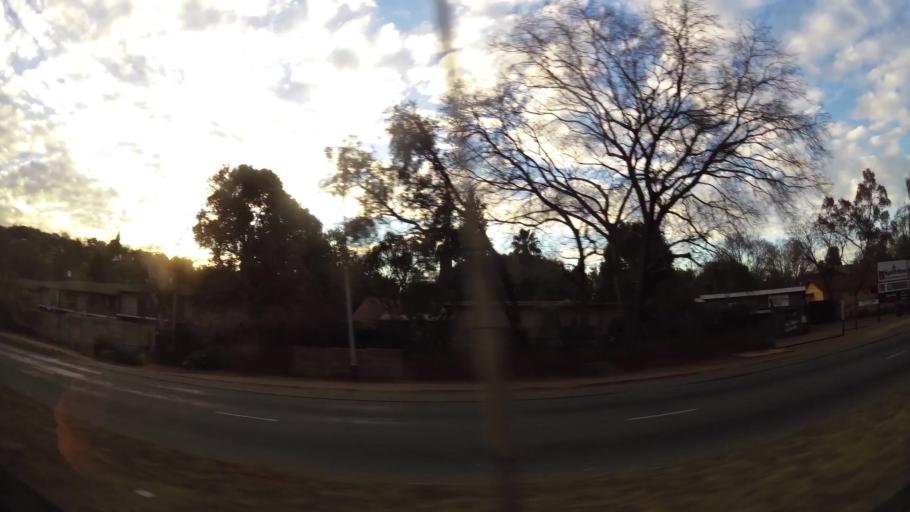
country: ZA
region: Gauteng
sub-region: City of Tshwane Metropolitan Municipality
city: Pretoria
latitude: -25.7411
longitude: 28.3068
